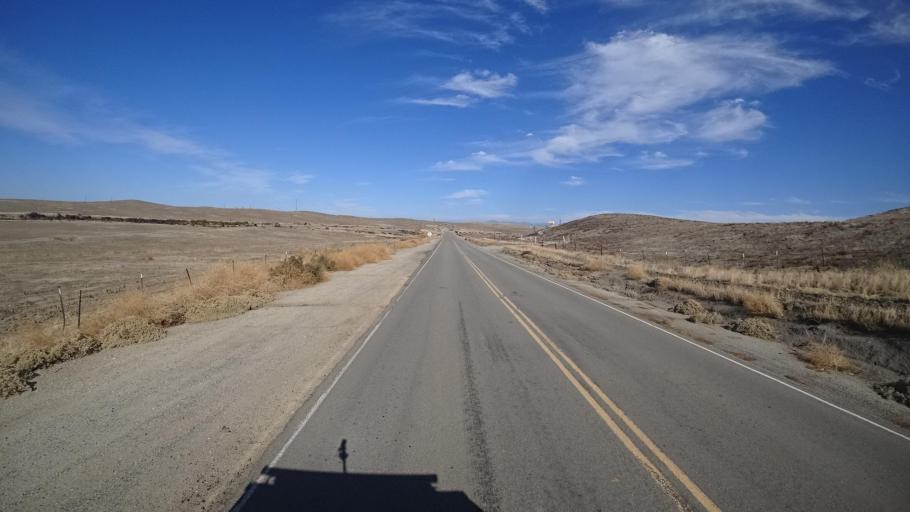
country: US
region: California
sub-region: Kern County
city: Oildale
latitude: 35.6049
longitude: -118.9503
